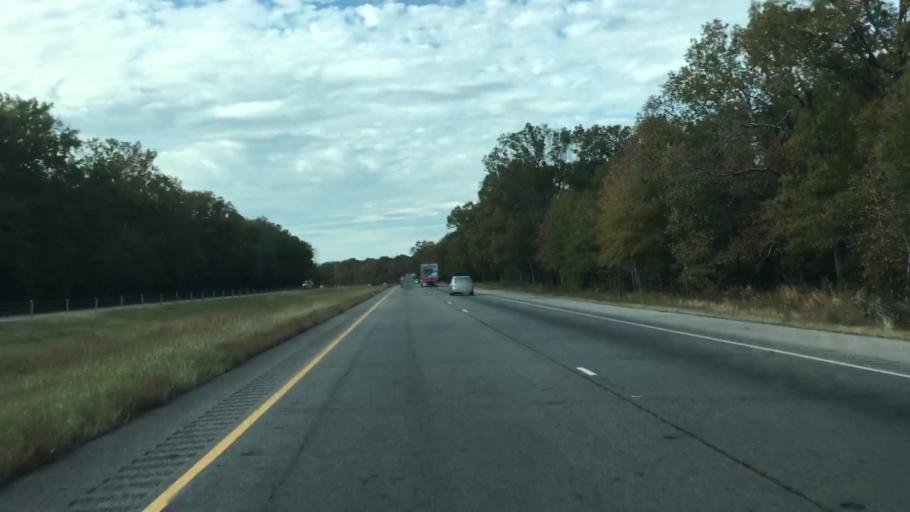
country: US
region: Arkansas
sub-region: Pope County
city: Atkins
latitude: 35.2420
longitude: -92.8603
